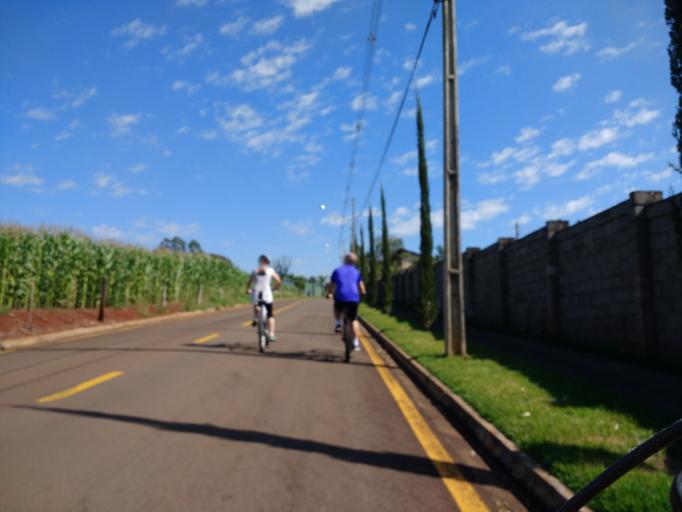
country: BR
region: Parana
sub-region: Londrina
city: Londrina
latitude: -23.3666
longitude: -51.1937
